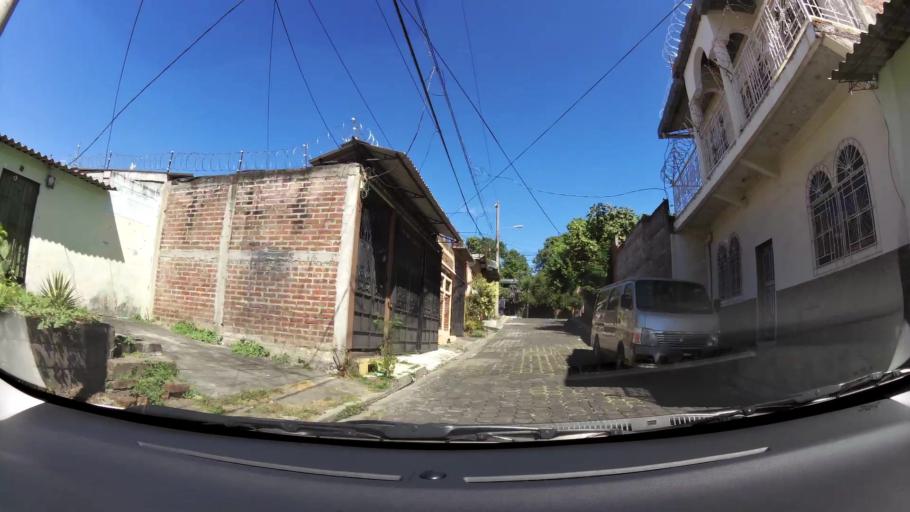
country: SV
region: San Miguel
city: San Miguel
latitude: 13.4818
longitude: -88.1707
